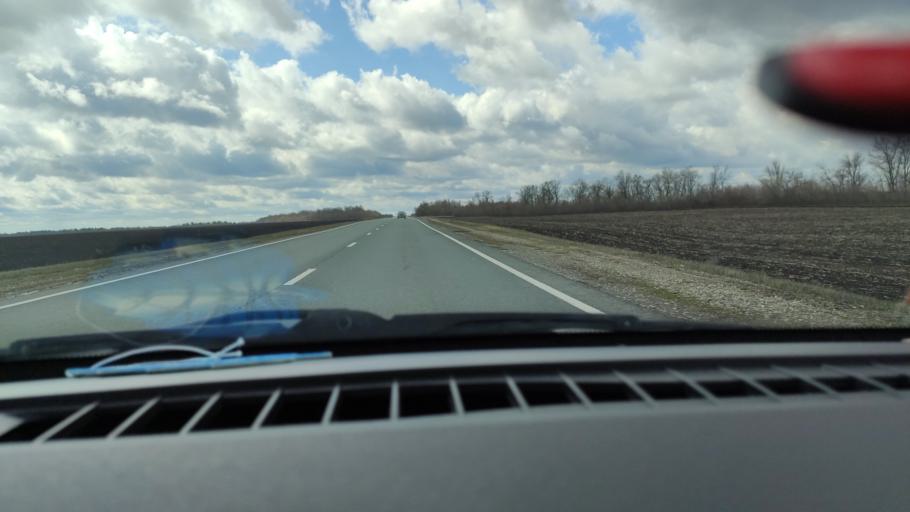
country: RU
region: Samara
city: Yelkhovka
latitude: 53.7709
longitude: 50.2338
